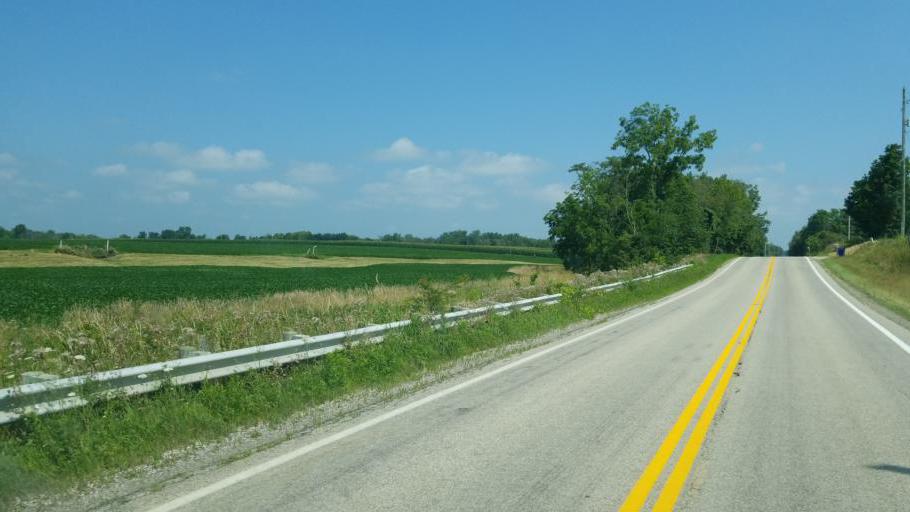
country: US
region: Ohio
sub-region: Crawford County
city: Galion
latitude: 40.8309
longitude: -82.8556
